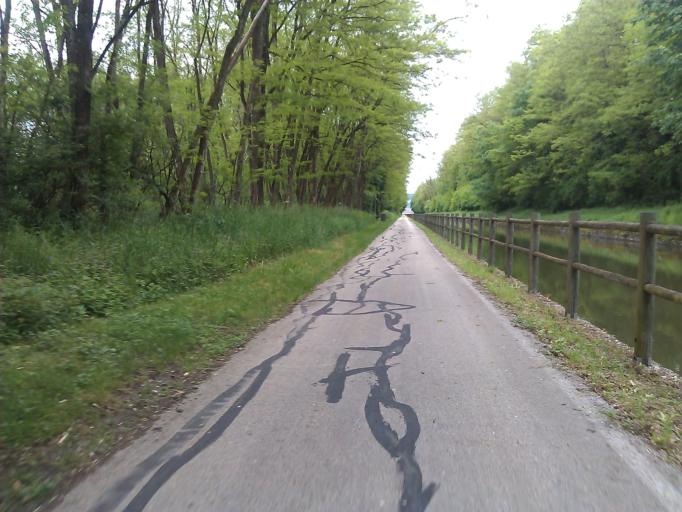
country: FR
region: Bourgogne
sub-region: Departement de Saone-et-Loire
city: Chagny
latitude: 46.8926
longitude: 4.7566
